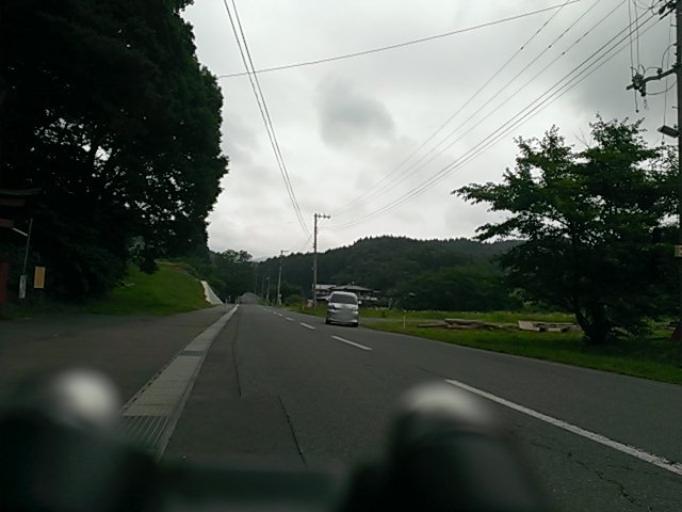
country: JP
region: Iwate
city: Morioka-shi
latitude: 39.8653
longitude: 141.1818
